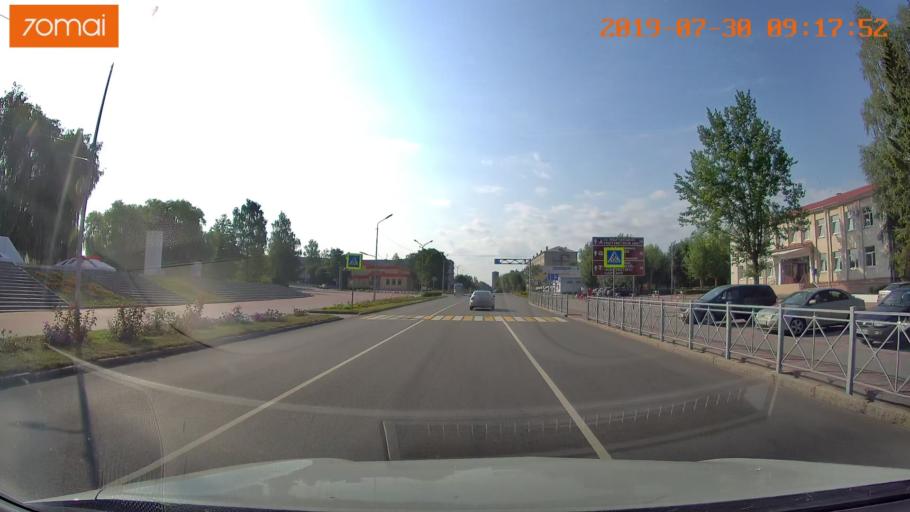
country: RU
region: Kaliningrad
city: Nesterov
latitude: 54.6319
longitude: 22.5710
